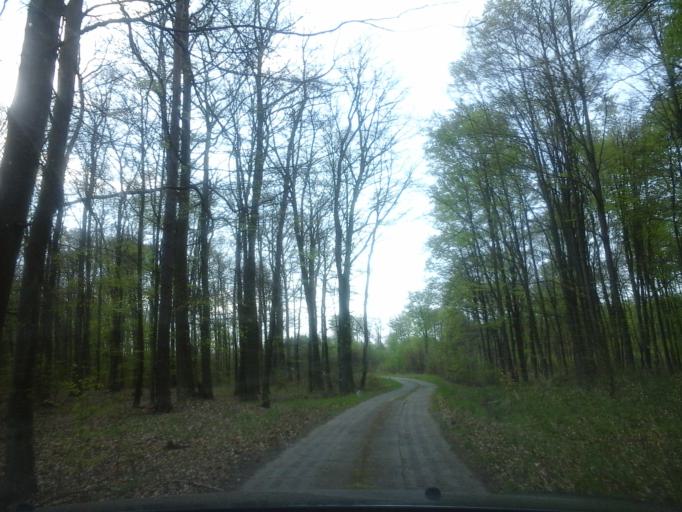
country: PL
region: West Pomeranian Voivodeship
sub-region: Powiat choszczenski
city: Krzecin
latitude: 53.0099
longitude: 15.4959
